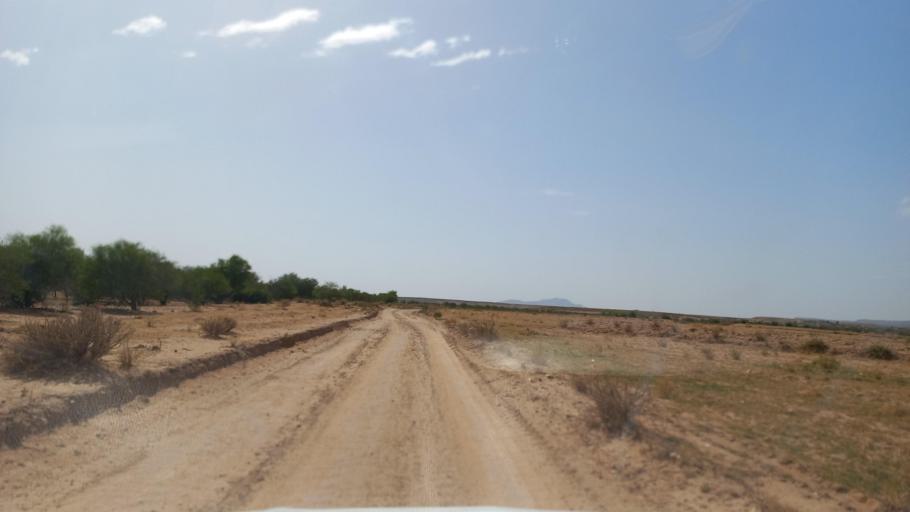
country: TN
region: Al Qasrayn
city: Kasserine
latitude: 35.2553
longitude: 8.9622
